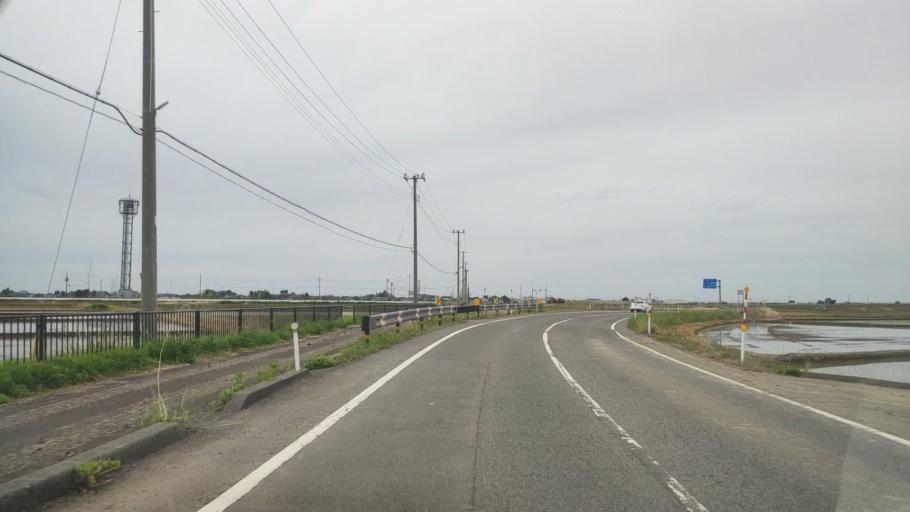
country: JP
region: Niigata
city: Shirone
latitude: 37.7364
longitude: 139.0800
